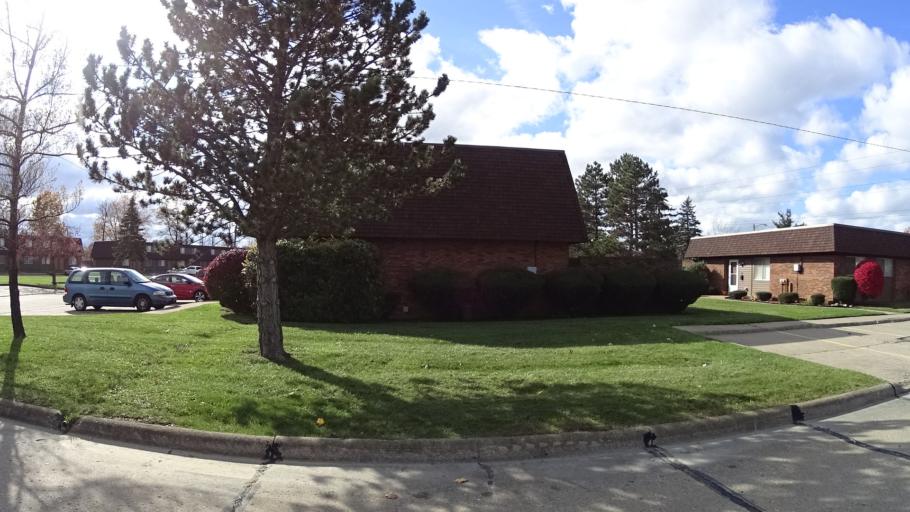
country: US
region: Ohio
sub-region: Lorain County
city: Lorain
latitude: 41.4298
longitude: -82.1986
